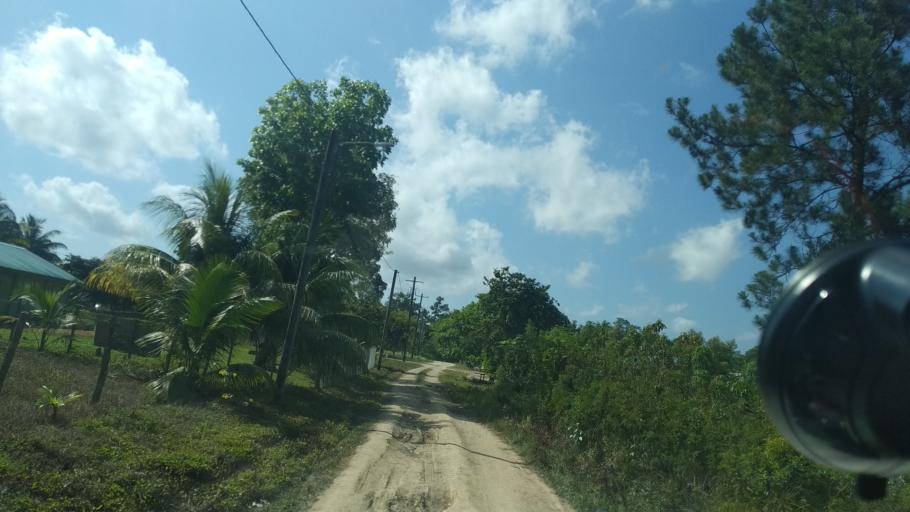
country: BZ
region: Stann Creek
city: Placencia
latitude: 16.4720
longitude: -88.6253
